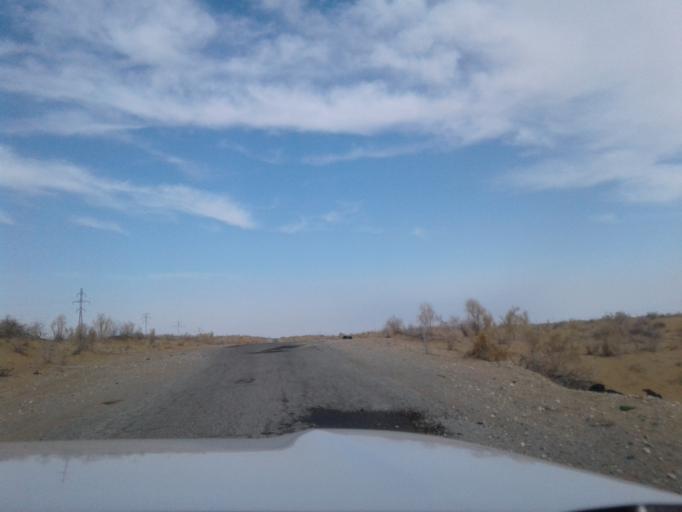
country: TM
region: Lebap
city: Gazojak
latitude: 40.4901
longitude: 61.1859
